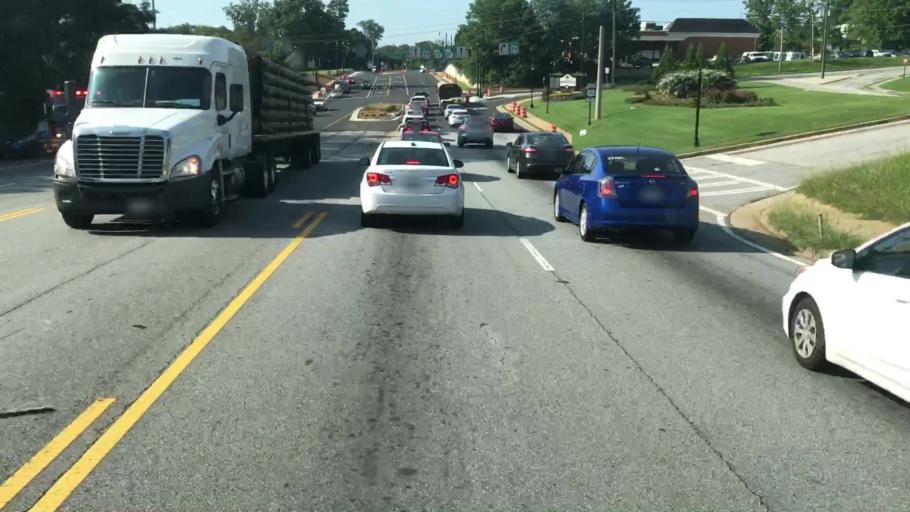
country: US
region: Georgia
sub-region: Gwinnett County
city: Lawrenceville
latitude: 33.9587
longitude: -83.9857
